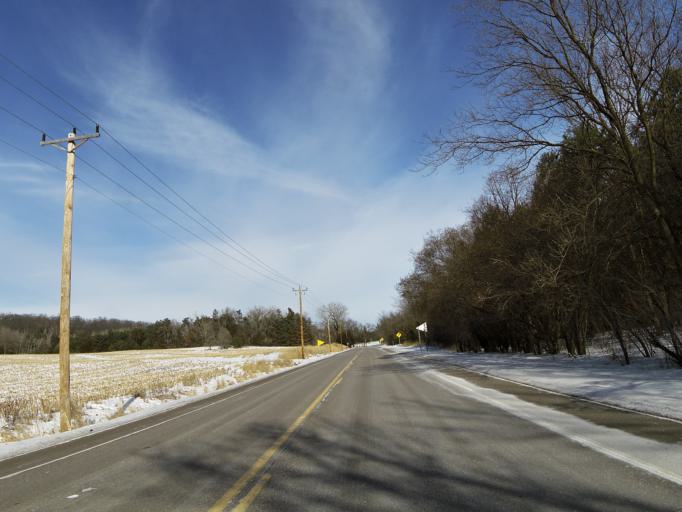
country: US
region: Minnesota
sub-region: Washington County
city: Afton
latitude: 44.8991
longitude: -92.8004
